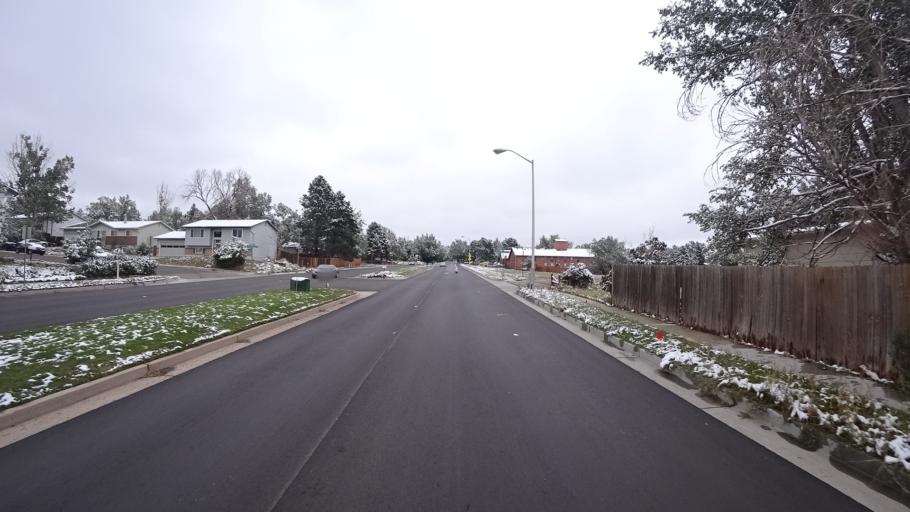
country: US
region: Colorado
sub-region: El Paso County
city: Cimarron Hills
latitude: 38.9050
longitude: -104.7649
